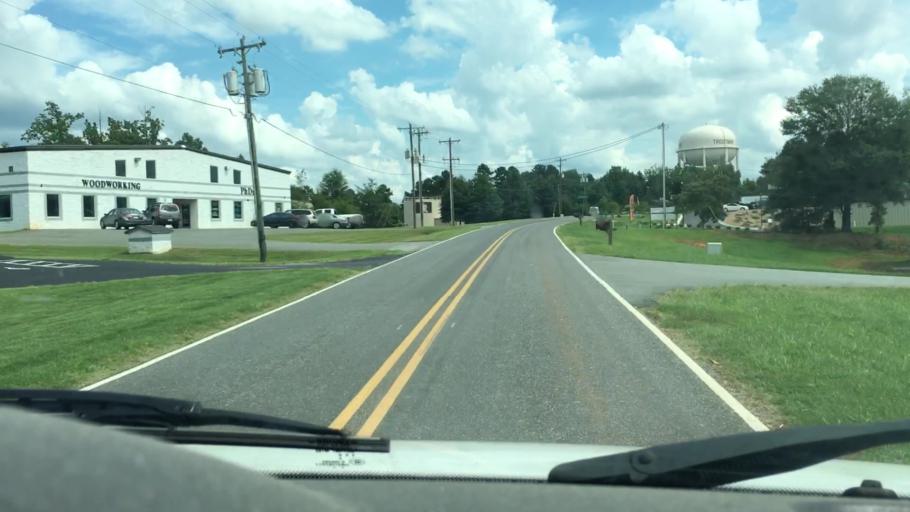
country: US
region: North Carolina
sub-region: Iredell County
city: Troutman
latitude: 35.6805
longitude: -80.8560
